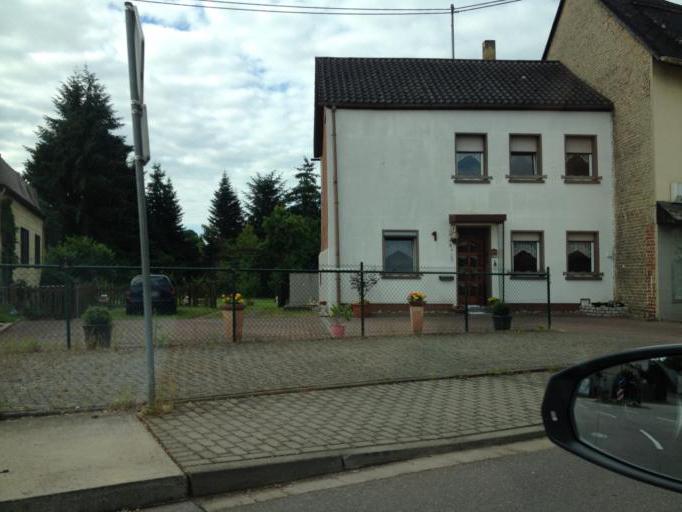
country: DE
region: Saarland
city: Lebach
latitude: 49.4518
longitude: 6.8970
